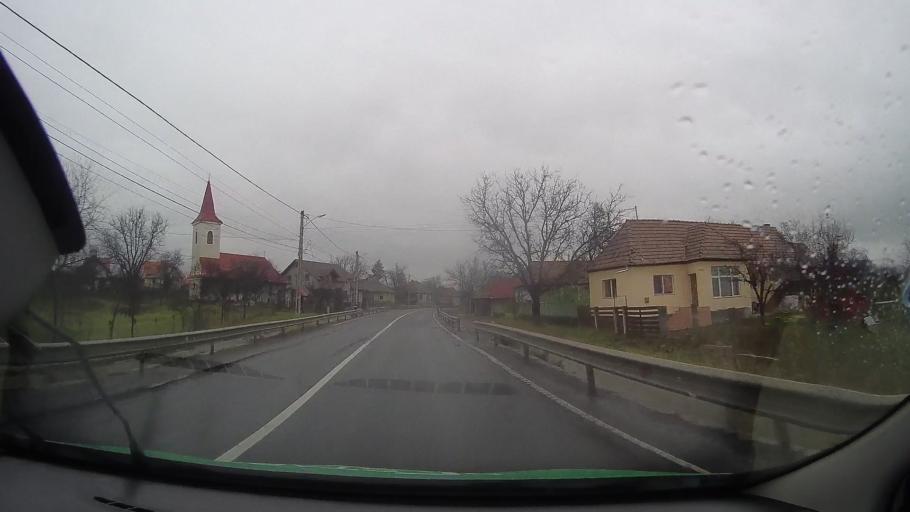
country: RO
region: Mures
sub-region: Comuna Brancovenesti
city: Brancovenesti
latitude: 46.8527
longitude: 24.7546
